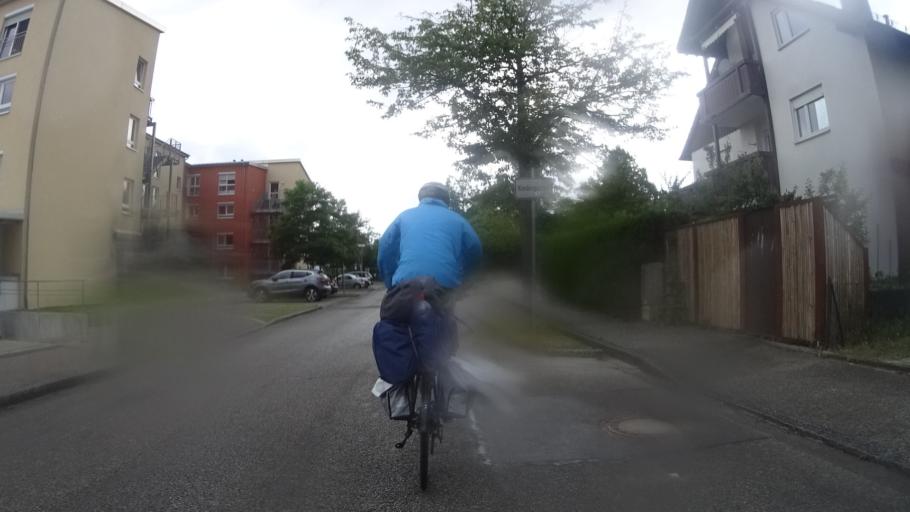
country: DE
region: Bavaria
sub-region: Upper Bavaria
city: Maisach
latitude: 48.2149
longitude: 11.2999
